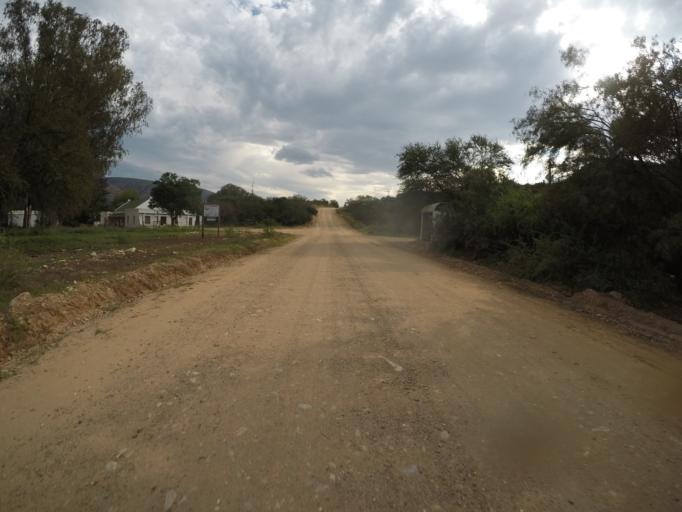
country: ZA
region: Eastern Cape
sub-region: Cacadu District Municipality
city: Kareedouw
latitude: -33.5830
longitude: 24.1645
